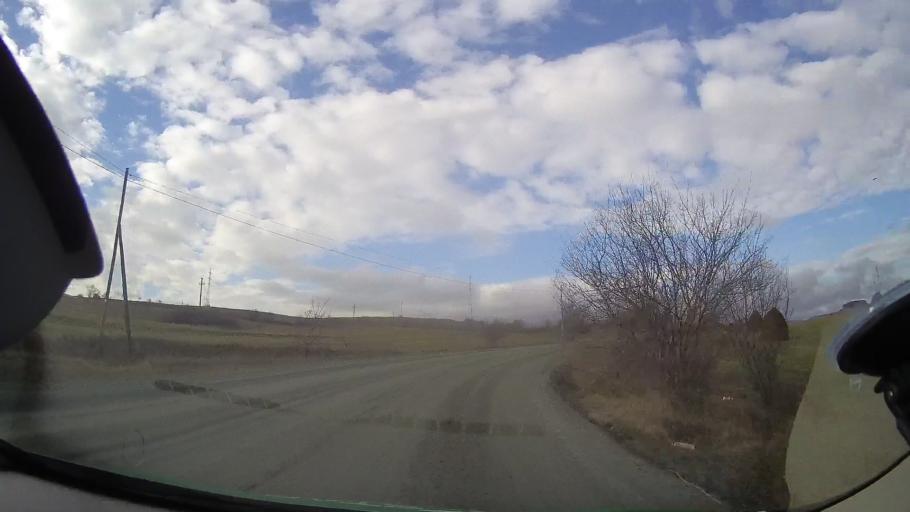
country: RO
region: Cluj
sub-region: Comuna Savadisla
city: Savadisla
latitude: 46.6392
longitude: 23.4548
